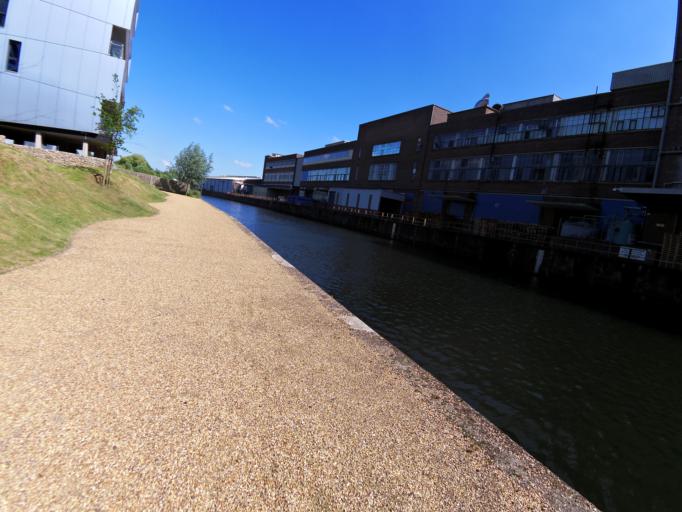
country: GB
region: England
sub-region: Norfolk
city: Thorpe Hamlet
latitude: 52.6203
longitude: 1.3103
